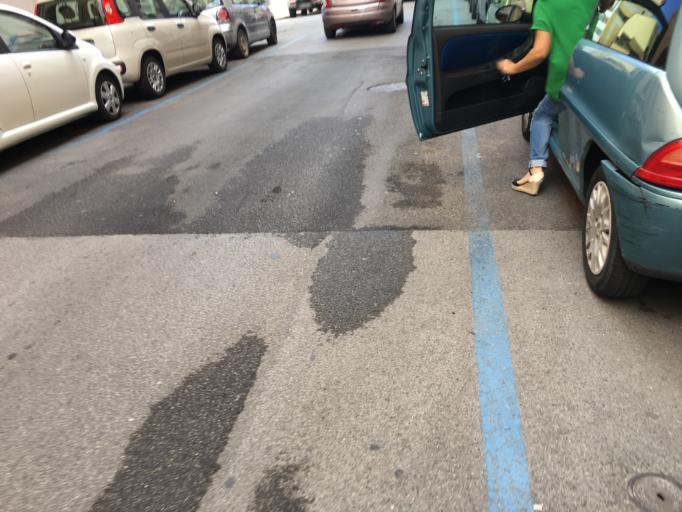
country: IT
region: Apulia
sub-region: Provincia di Bari
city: Bari
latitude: 41.1225
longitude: 16.8769
